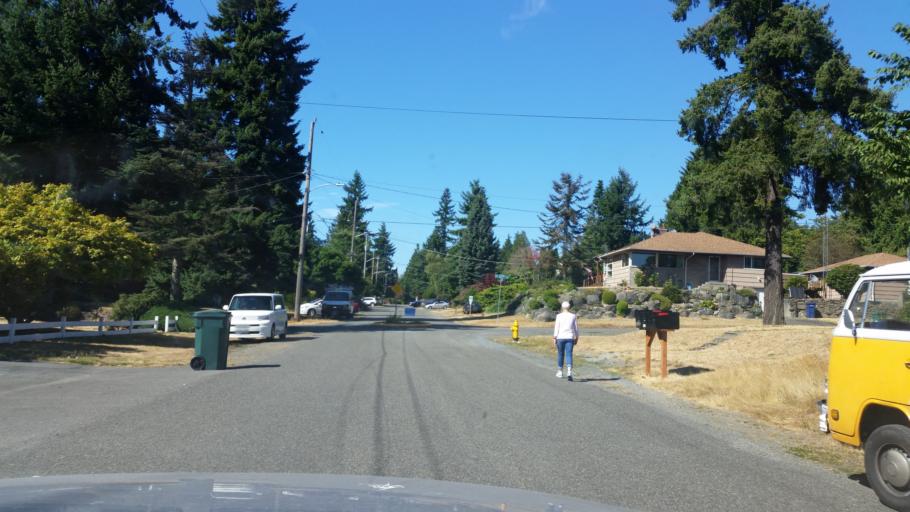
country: US
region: Washington
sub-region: King County
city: Shoreline
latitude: 47.7211
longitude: -122.3596
